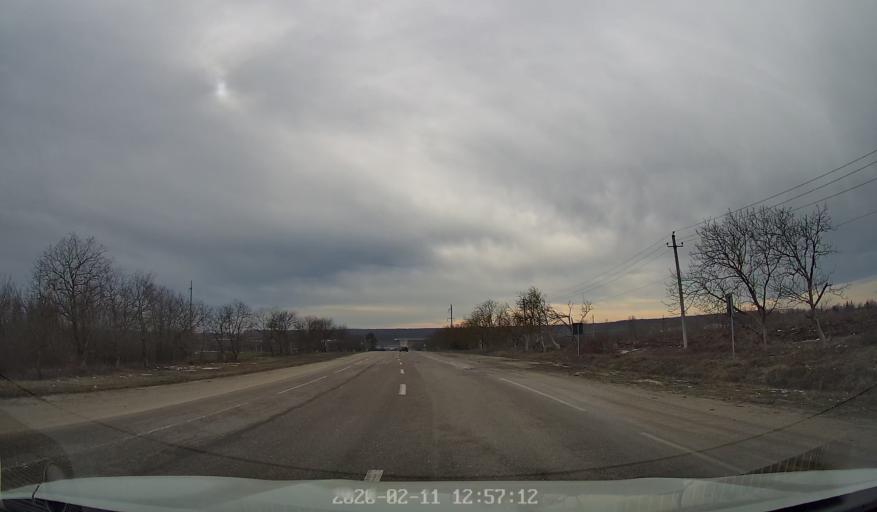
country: MD
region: Briceni
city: Briceni
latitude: 48.3434
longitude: 27.0693
